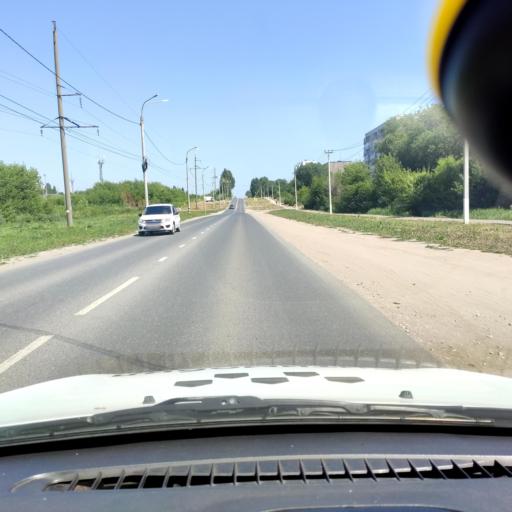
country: RU
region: Samara
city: Zhigulevsk
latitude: 53.4099
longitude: 49.5256
